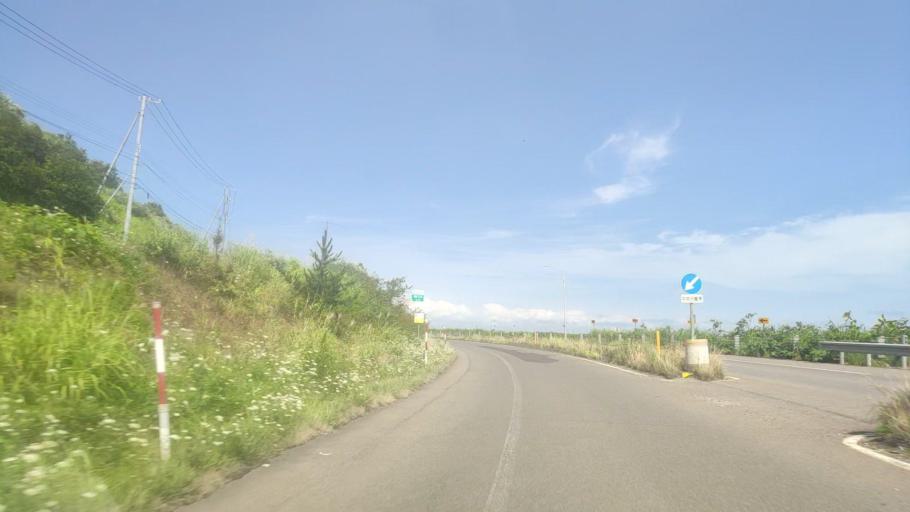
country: JP
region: Hokkaido
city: Nanae
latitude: 42.1969
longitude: 140.4196
